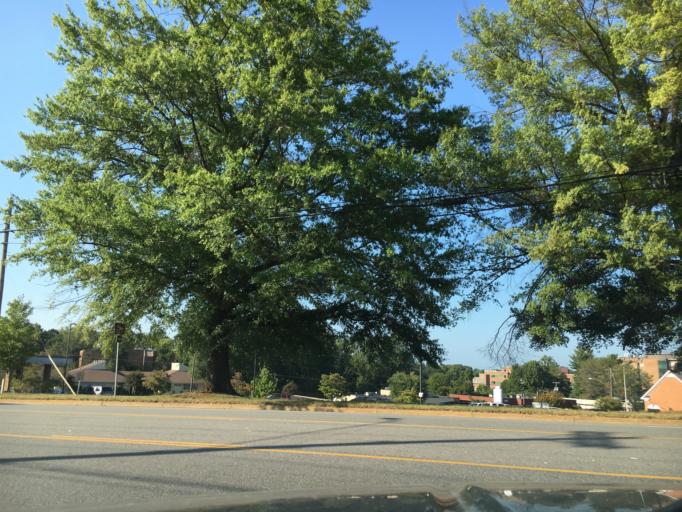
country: US
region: Virginia
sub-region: City of Lynchburg
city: West Lynchburg
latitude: 37.4128
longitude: -79.1738
